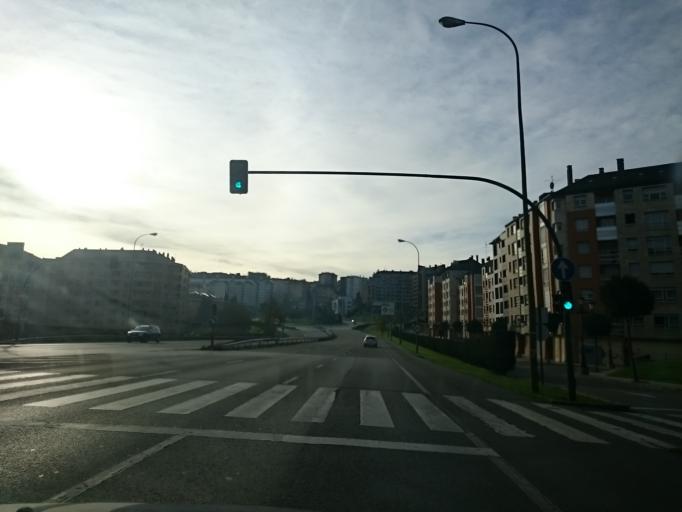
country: ES
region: Asturias
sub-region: Province of Asturias
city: Oviedo
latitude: 43.3565
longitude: -5.8394
